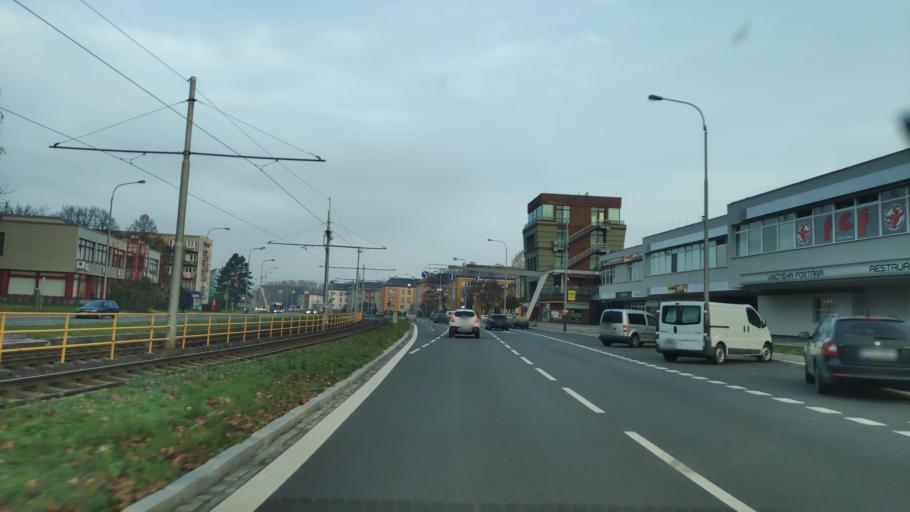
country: CZ
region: Moravskoslezsky
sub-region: Okres Ostrava-Mesto
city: Ostrava
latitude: 49.7874
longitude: 18.2561
